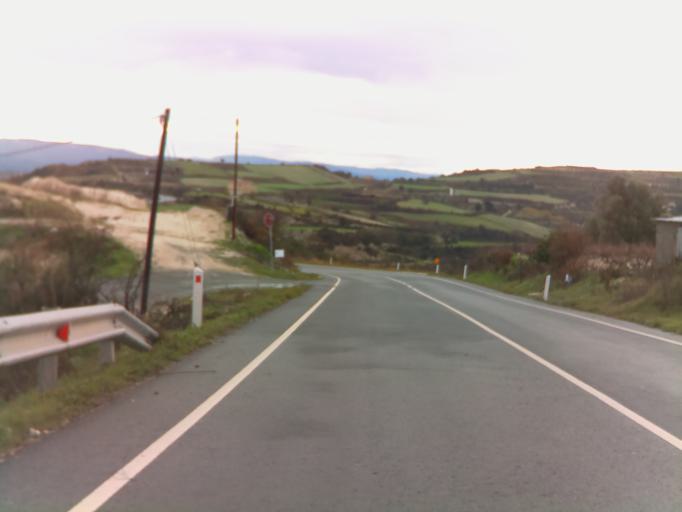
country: CY
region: Pafos
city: Tala
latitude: 34.8976
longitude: 32.4547
